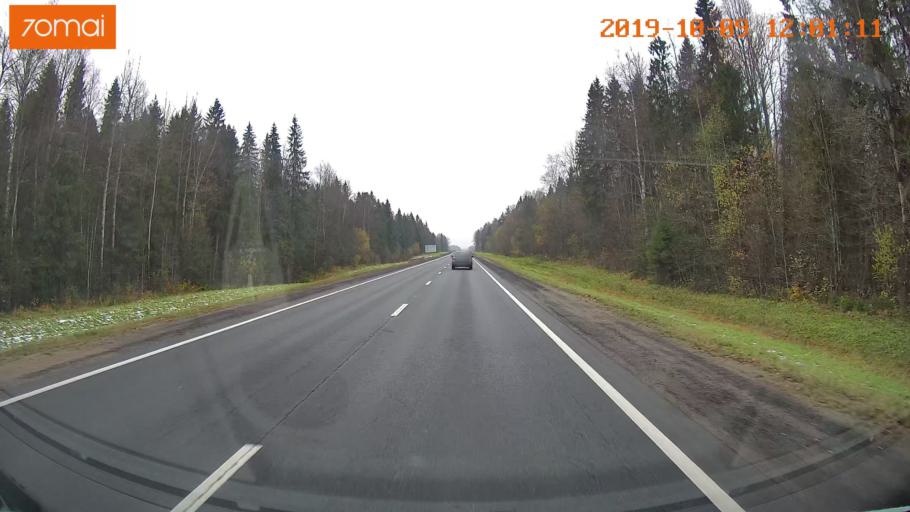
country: RU
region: Vologda
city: Gryazovets
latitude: 58.6910
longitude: 40.3022
